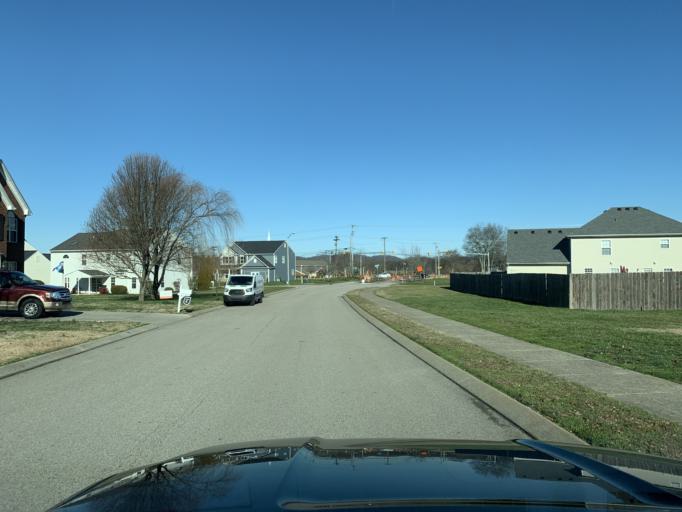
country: US
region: Tennessee
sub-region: Maury County
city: Spring Hill
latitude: 35.7513
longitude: -86.9107
